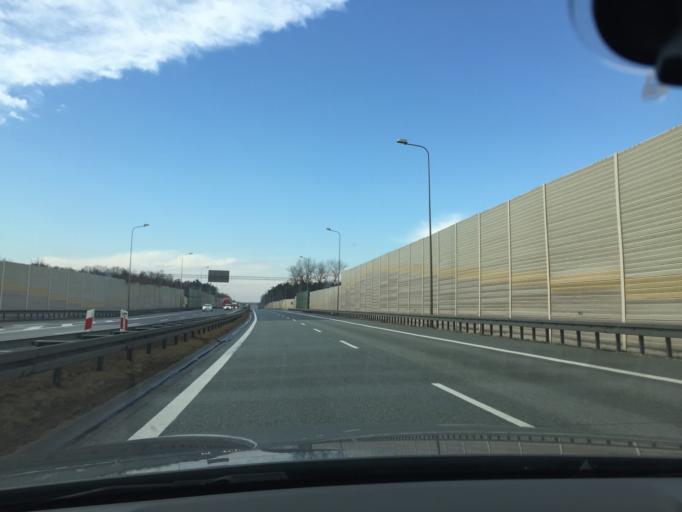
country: PL
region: Lodz Voivodeship
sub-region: Powiat skierniewicki
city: Kowiesy
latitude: 51.8400
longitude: 20.3491
